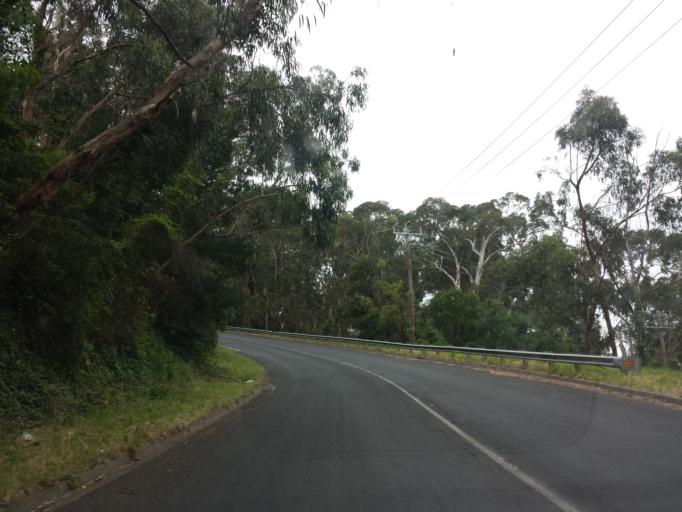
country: AU
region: Victoria
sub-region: Yarra Ranges
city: Tremont
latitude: -37.9152
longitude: 145.3256
